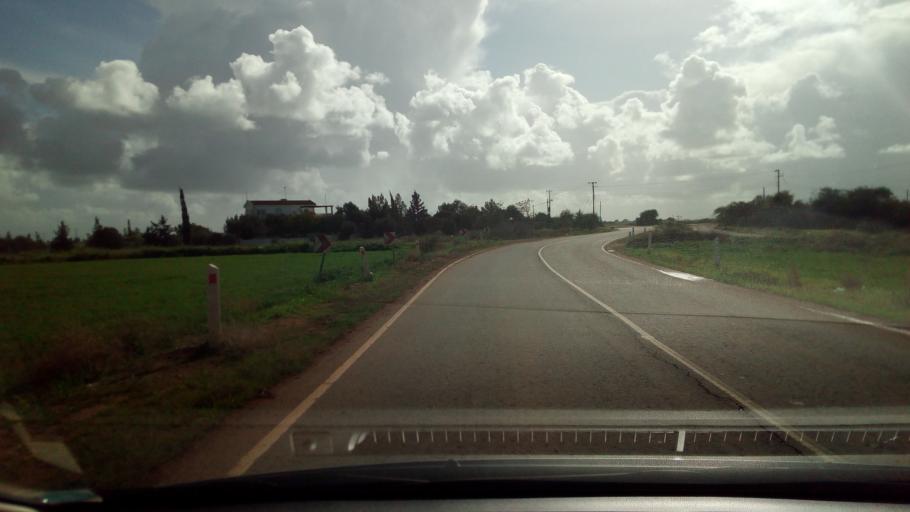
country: CY
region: Ammochostos
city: Avgorou
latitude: 35.0501
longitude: 33.8149
